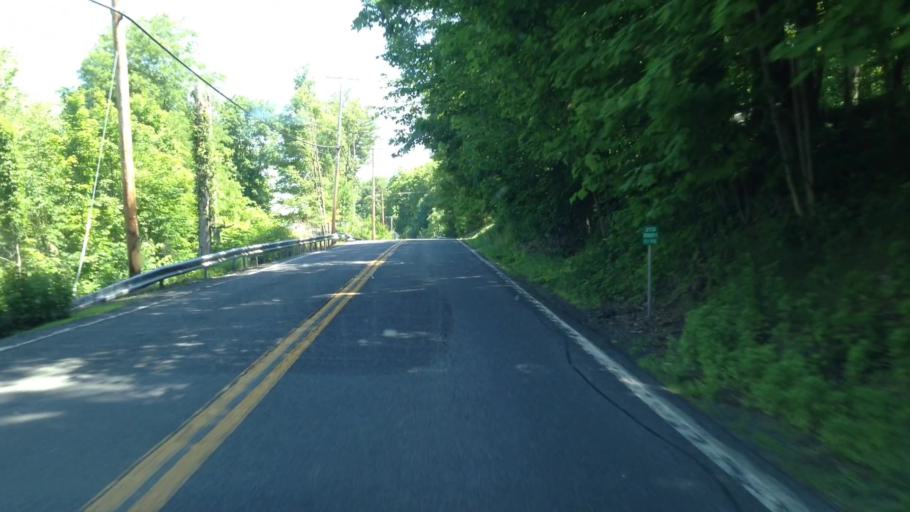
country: US
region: New York
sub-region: Ulster County
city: Tillson
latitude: 41.8320
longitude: -74.0460
